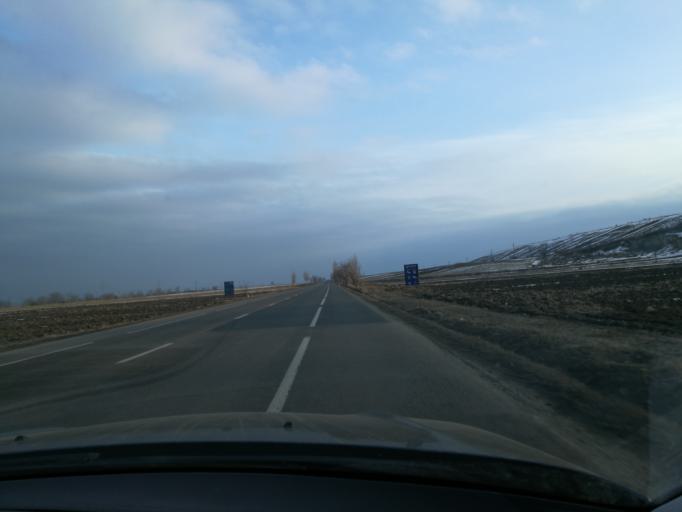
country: RO
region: Bacau
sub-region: Comuna Orbeni
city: Orbeni
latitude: 46.3003
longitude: 27.0342
